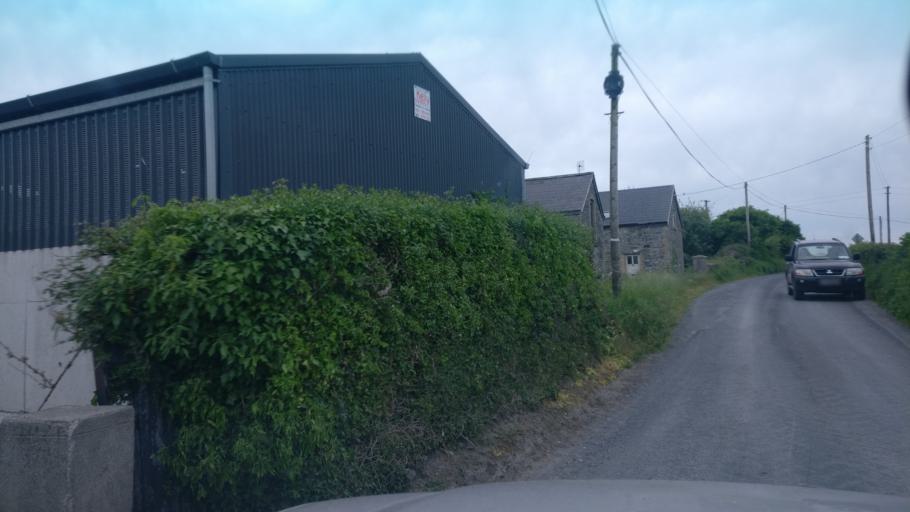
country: IE
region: Connaught
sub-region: County Galway
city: Portumna
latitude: 53.1451
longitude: -8.2876
